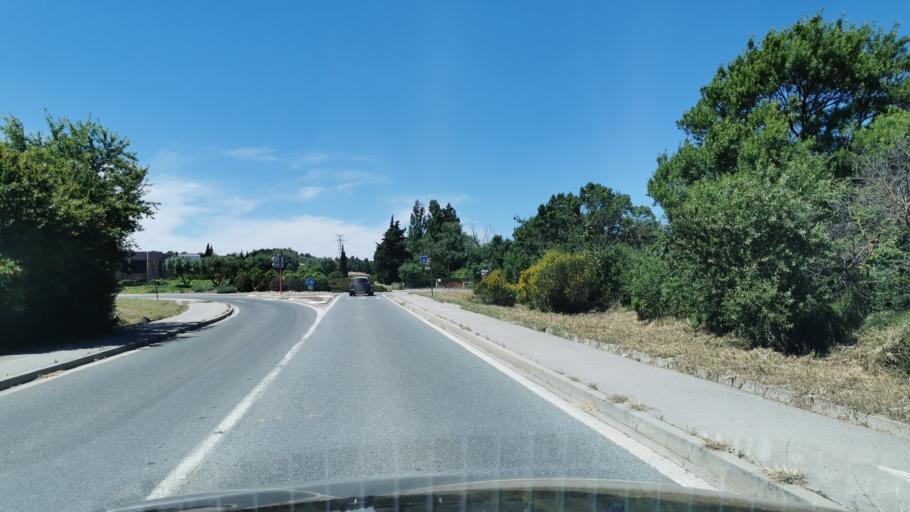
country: FR
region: Languedoc-Roussillon
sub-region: Departement de l'Aude
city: Narbonne
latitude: 43.1980
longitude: 2.9745
